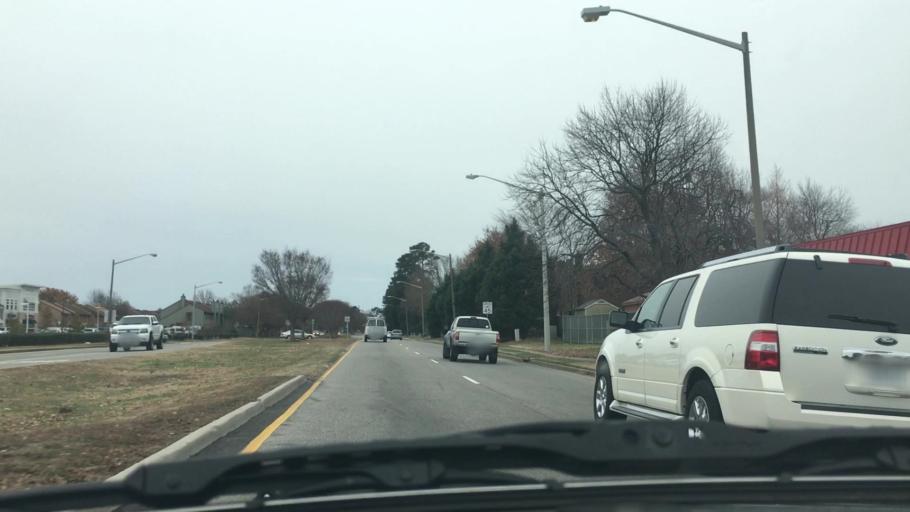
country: US
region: Virginia
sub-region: City of Chesapeake
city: Chesapeake
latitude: 36.8217
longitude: -76.1270
